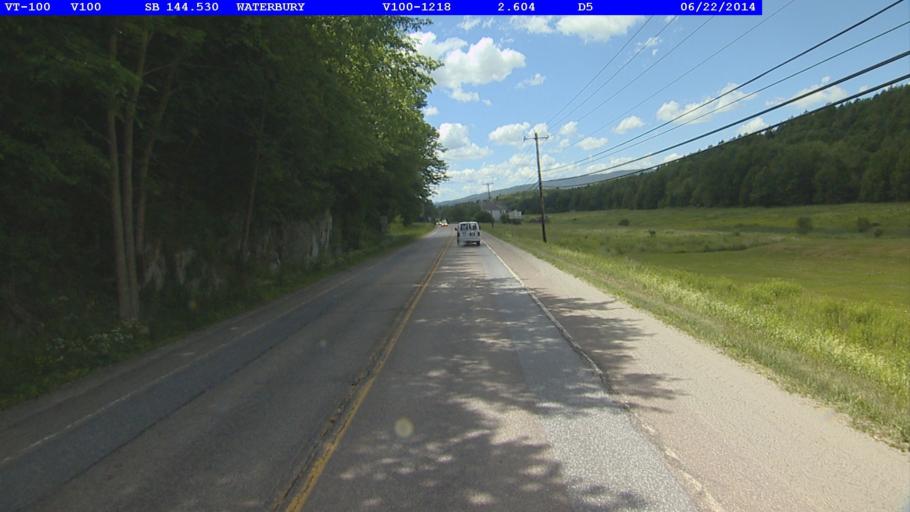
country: US
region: Vermont
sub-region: Washington County
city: Waterbury
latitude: 44.3685
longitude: -72.7288
